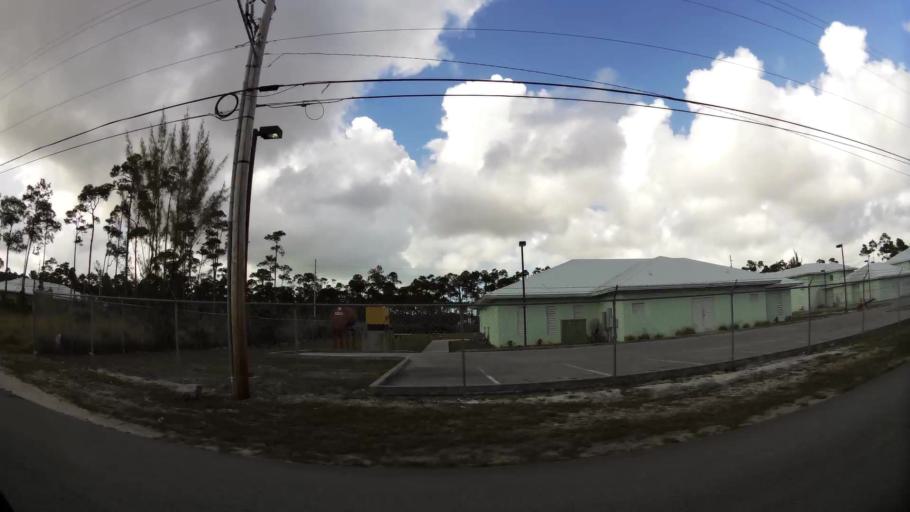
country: BS
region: Freeport
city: Freeport
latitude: 26.5284
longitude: -78.7048
